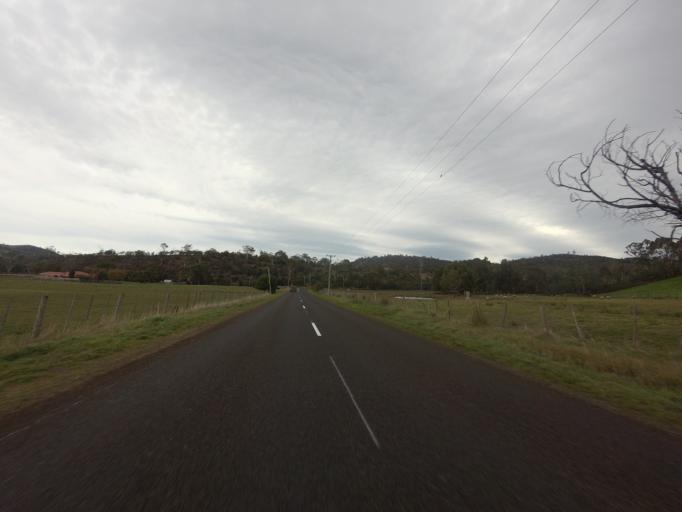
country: AU
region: Tasmania
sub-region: Brighton
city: Bridgewater
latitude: -42.6751
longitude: 147.1548
